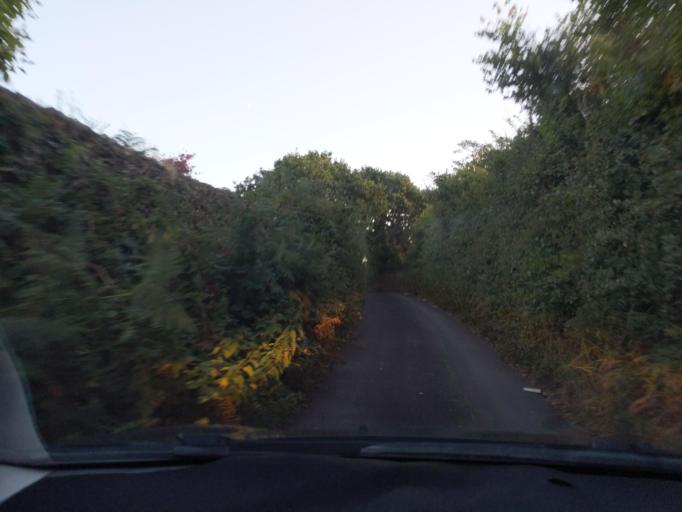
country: GB
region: England
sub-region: Plymouth
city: Plymstock
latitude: 50.3566
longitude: -4.0903
